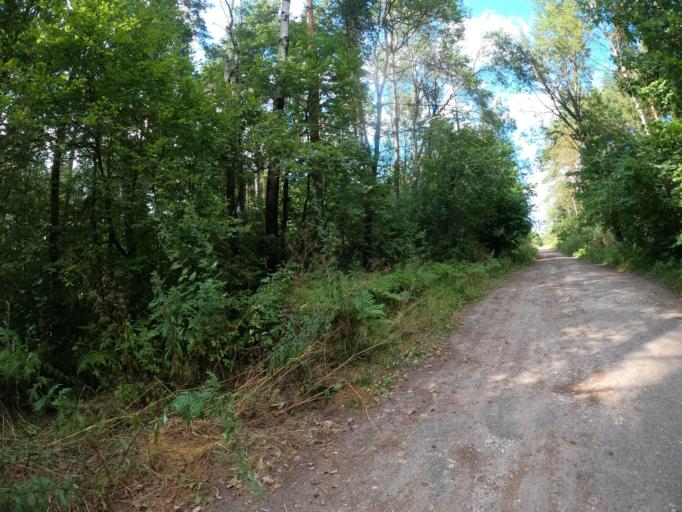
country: RU
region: Moskovskaya
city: Lopatinskiy
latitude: 55.3857
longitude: 38.7091
